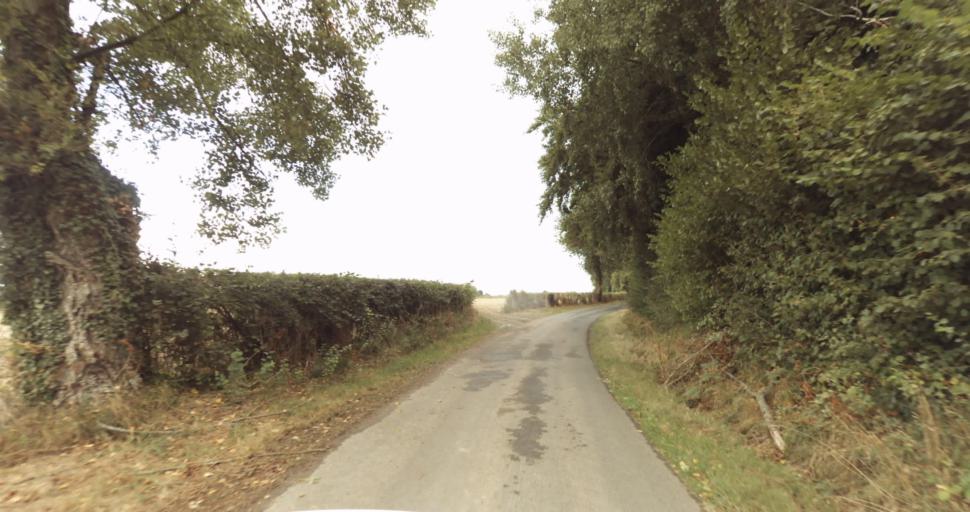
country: FR
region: Lower Normandy
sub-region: Departement de l'Orne
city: Vimoutiers
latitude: 48.9329
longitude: 0.1464
